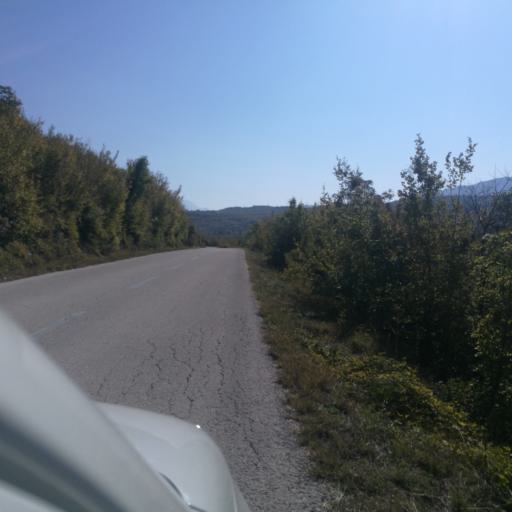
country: HR
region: Splitsko-Dalmatinska
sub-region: Grad Omis
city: Omis
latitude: 43.5202
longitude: 16.7541
